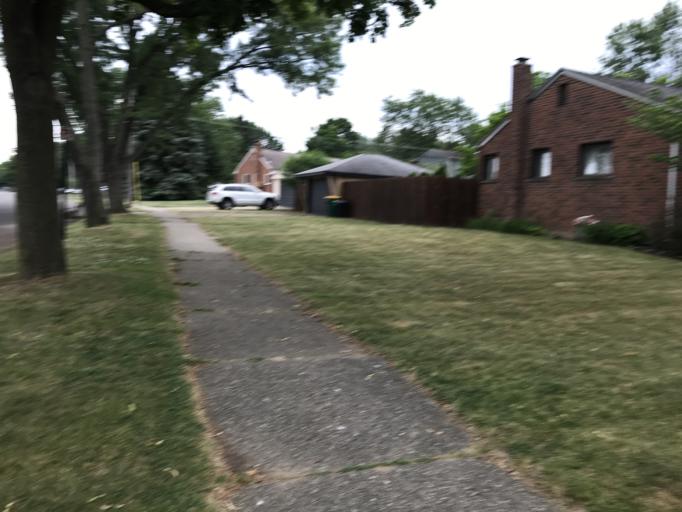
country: US
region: Michigan
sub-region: Oakland County
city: Farmington
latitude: 42.4668
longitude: -83.3636
